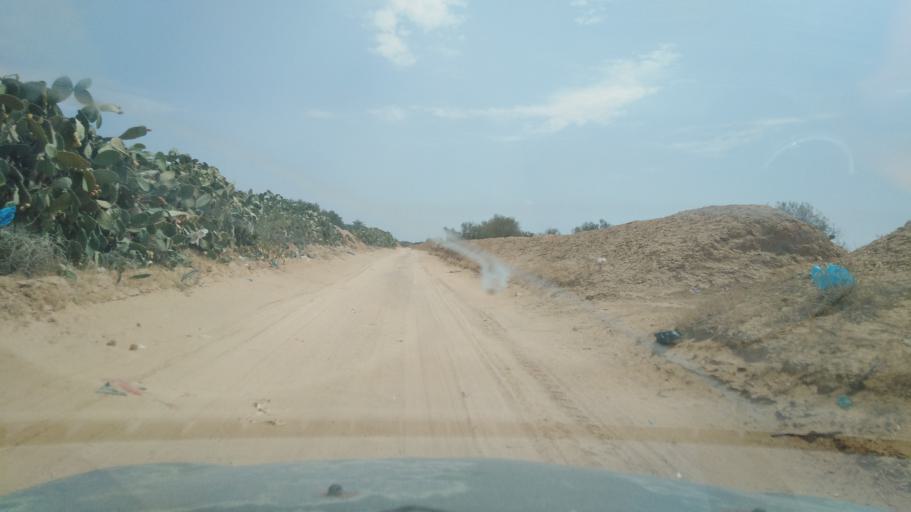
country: TN
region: Safaqis
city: Sfax
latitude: 34.7386
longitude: 10.5516
